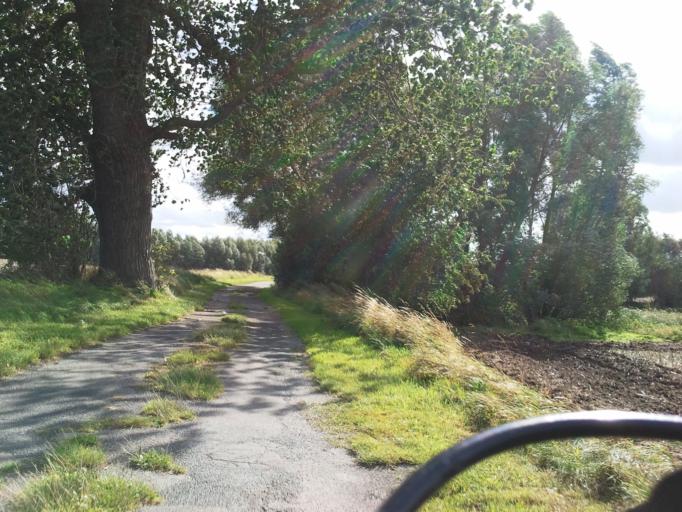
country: DE
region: Mecklenburg-Vorpommern
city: Dierkow-West
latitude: 54.1159
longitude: 12.1230
